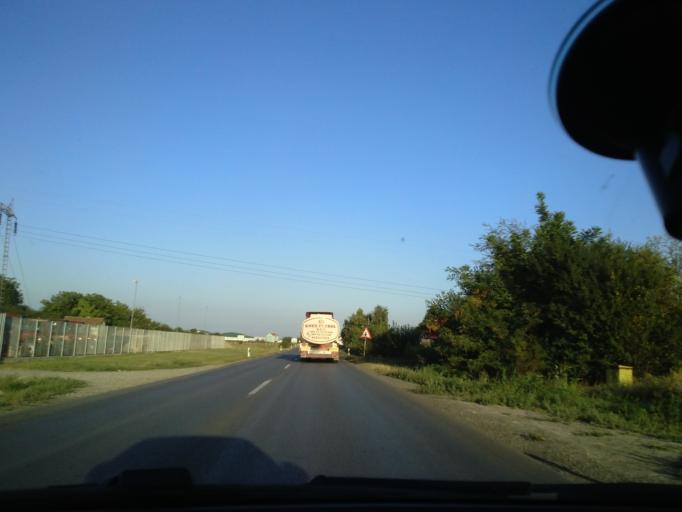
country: RS
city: Rumenka
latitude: 45.2880
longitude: 19.7552
